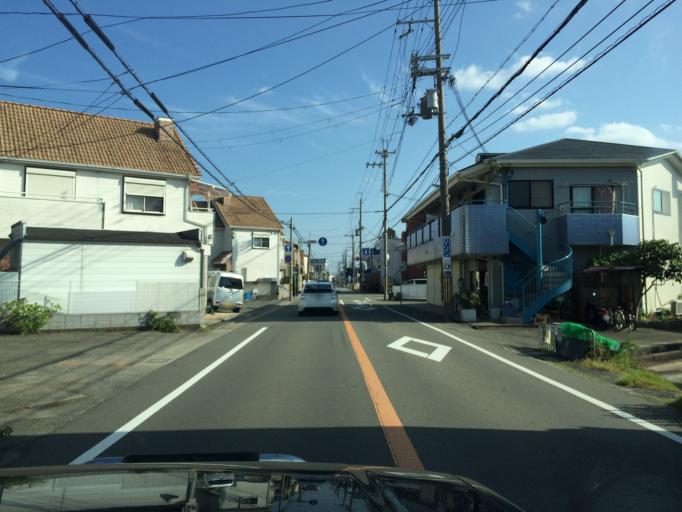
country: JP
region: Hyogo
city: Itami
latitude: 34.7683
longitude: 135.4073
